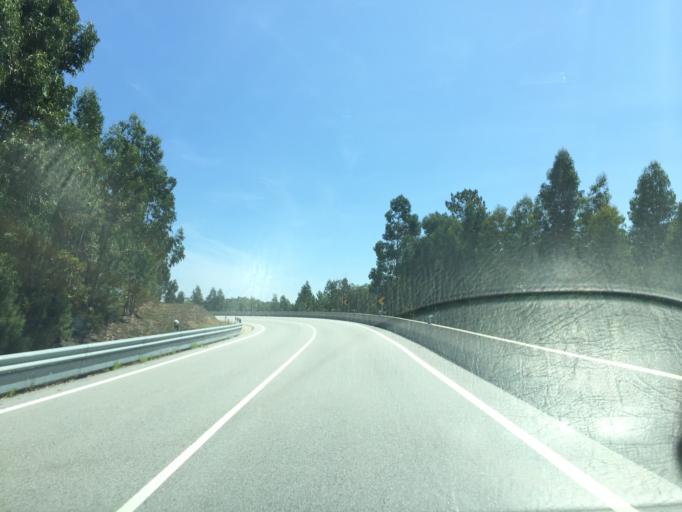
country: PT
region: Castelo Branco
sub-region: Proenca-A-Nova
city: Proenca-a-Nova
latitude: 39.7833
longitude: -7.8745
